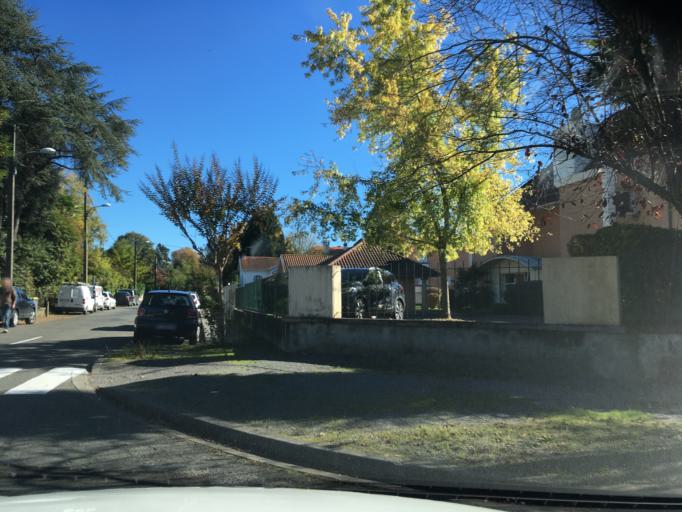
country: FR
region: Aquitaine
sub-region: Departement des Pyrenees-Atlantiques
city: Pau
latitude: 43.3024
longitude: -0.3483
